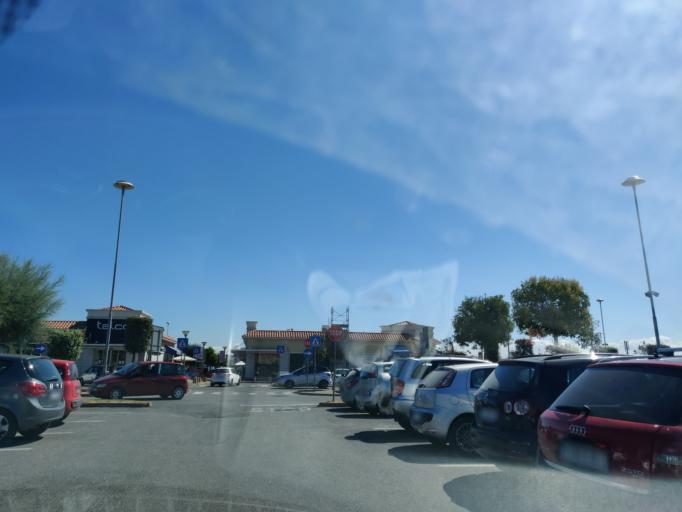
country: IT
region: Latium
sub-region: Citta metropolitana di Roma Capitale
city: Npp 23 (Parco Leonardo)
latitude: 41.8085
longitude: 12.2995
